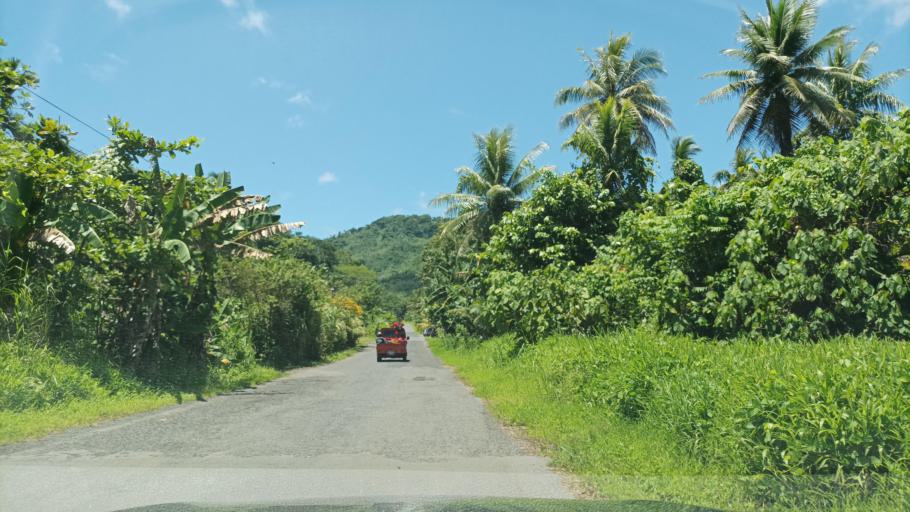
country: FM
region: Pohnpei
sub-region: Madolenihm Municipality
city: Madolenihm Municipality Government
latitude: 6.9188
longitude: 158.2892
